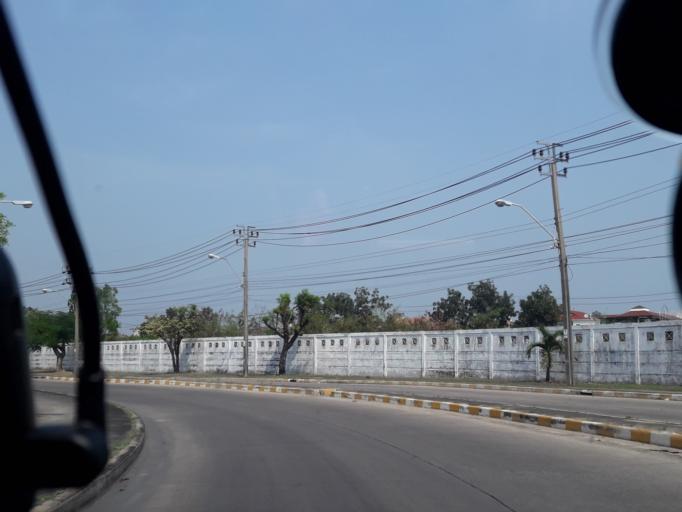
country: TH
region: Bangkok
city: Khan Na Yao
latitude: 13.8444
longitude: 100.6994
